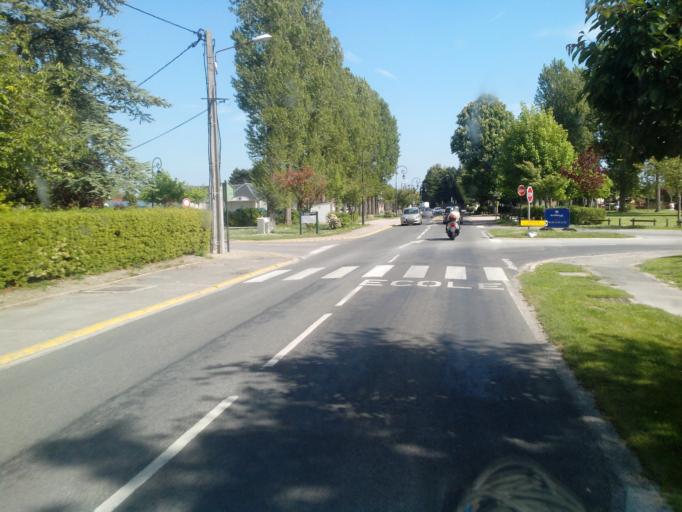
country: FR
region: Nord-Pas-de-Calais
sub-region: Departement du Pas-de-Calais
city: Groffliers
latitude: 50.3848
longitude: 1.6150
